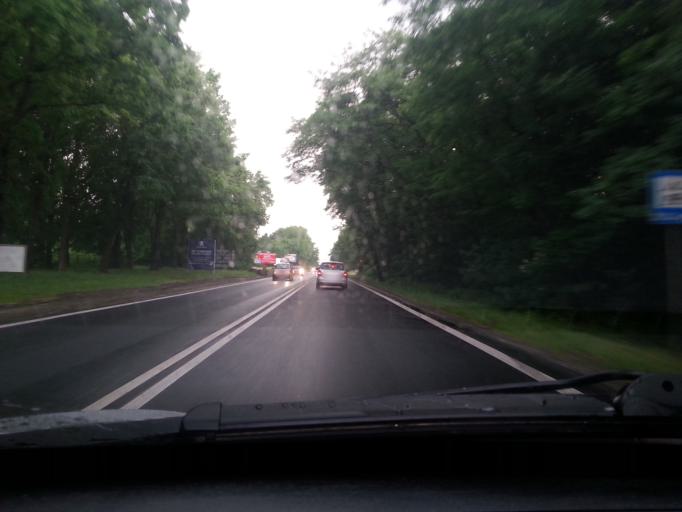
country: PL
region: Lodz Voivodeship
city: Lodz
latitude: 51.8167
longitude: 19.5044
